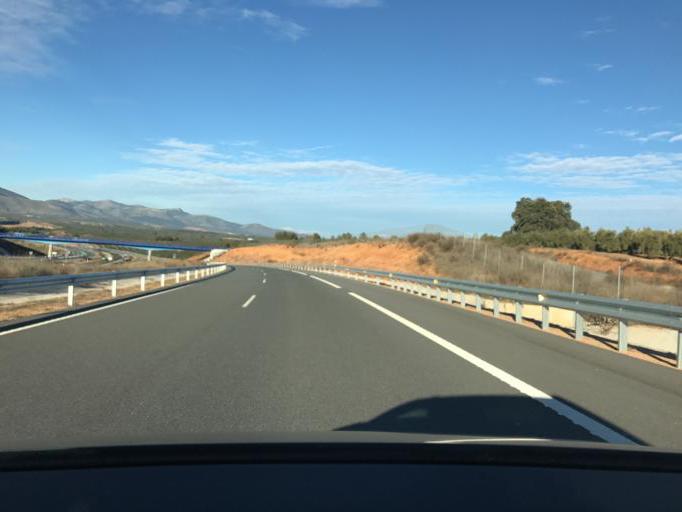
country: ES
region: Andalusia
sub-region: Provincia de Granada
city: Albolote
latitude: 37.2664
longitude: -3.6588
